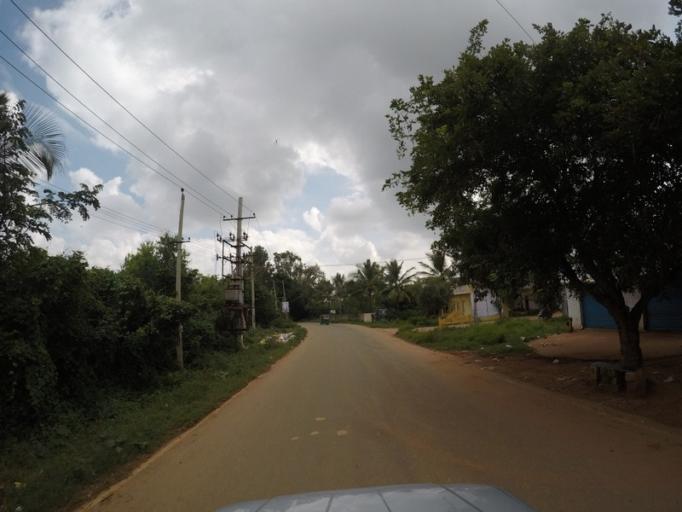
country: IN
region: Karnataka
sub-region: Bangalore Urban
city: Yelahanka
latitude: 13.1087
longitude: 77.5279
